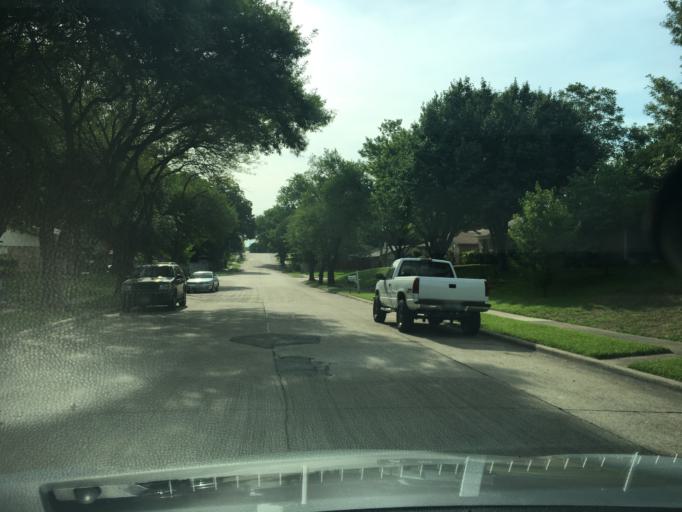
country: US
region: Texas
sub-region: Collin County
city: Plano
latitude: 32.9690
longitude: -96.6726
